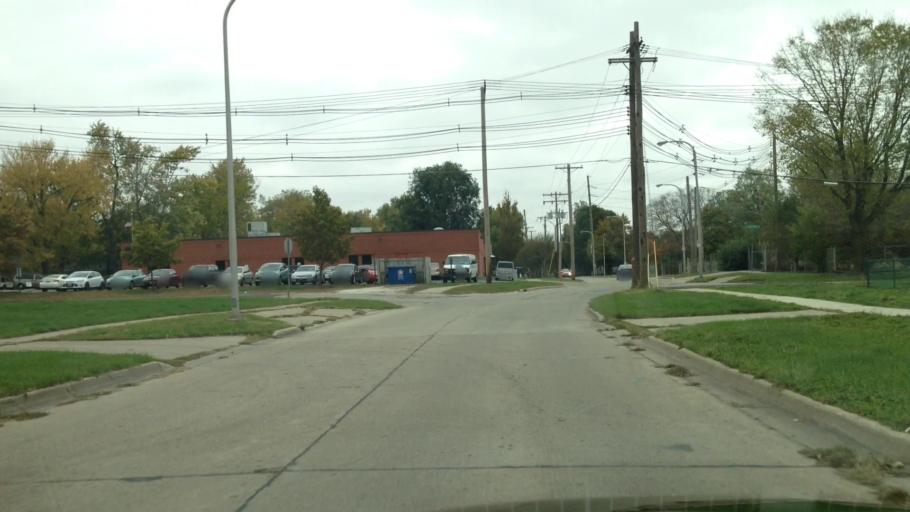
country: US
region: Illinois
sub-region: Champaign County
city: Champaign
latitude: 40.1230
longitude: -88.2412
